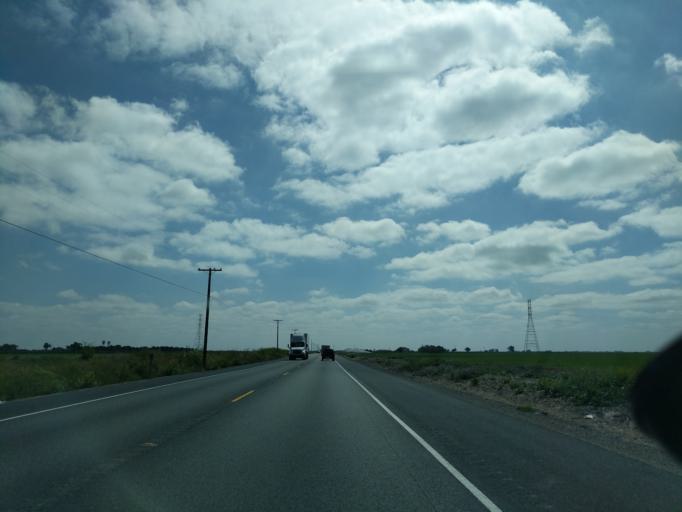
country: US
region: California
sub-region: San Joaquin County
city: Country Club
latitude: 37.9269
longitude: -121.4121
